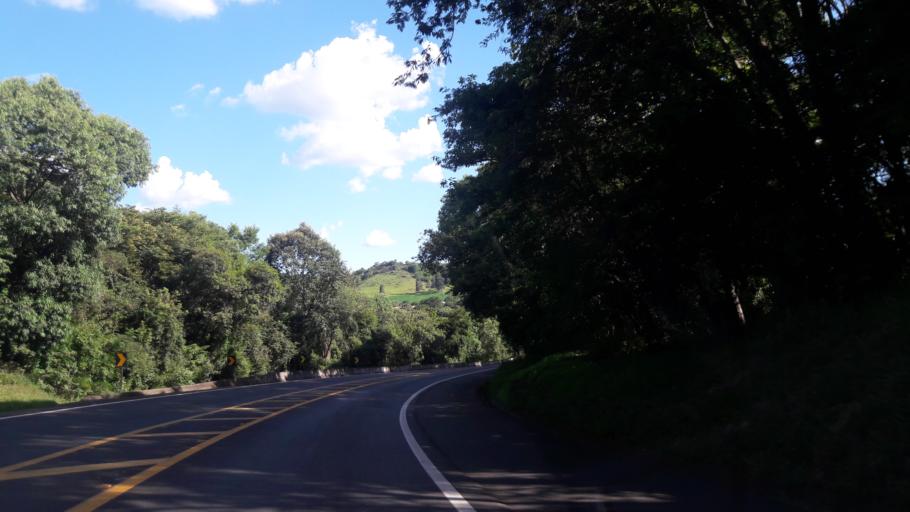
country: BR
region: Parana
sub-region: Laranjeiras Do Sul
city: Laranjeiras do Sul
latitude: -25.4189
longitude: -52.0325
